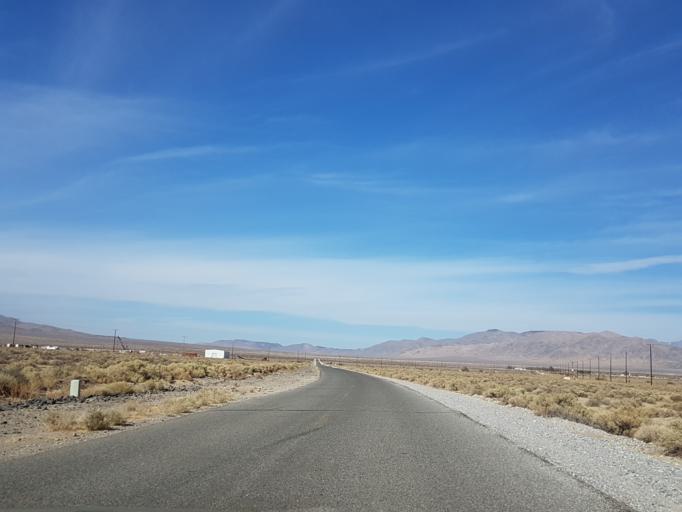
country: US
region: California
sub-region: San Bernardino County
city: Searles Valley
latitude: 35.8112
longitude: -117.3440
